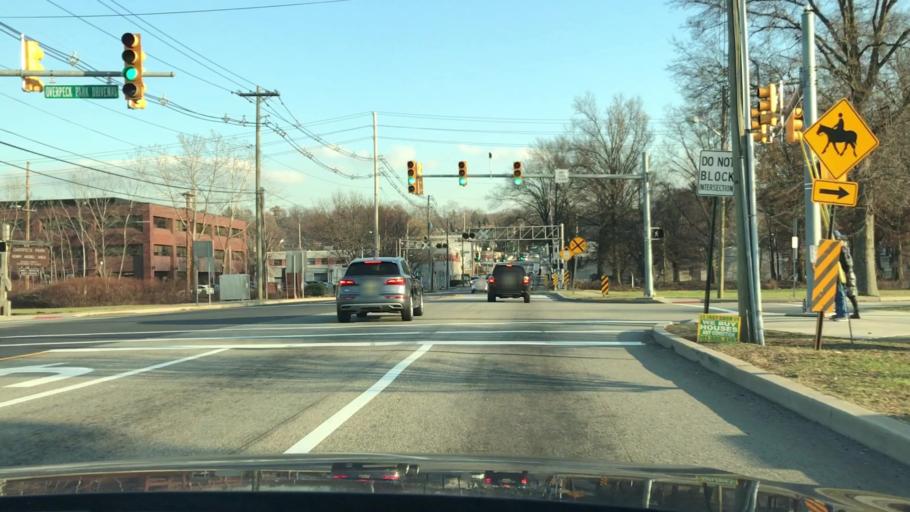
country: US
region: New Jersey
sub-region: Bergen County
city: Leonia
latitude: 40.8654
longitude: -73.9957
